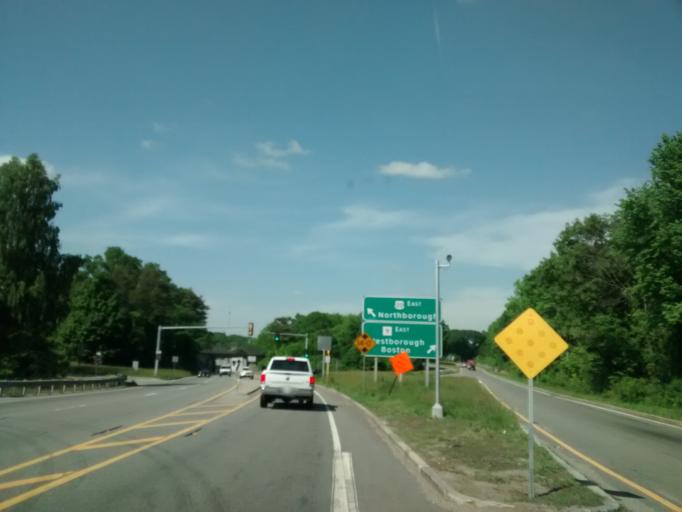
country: US
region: Massachusetts
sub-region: Worcester County
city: Shrewsbury
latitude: 42.2806
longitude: -71.6713
